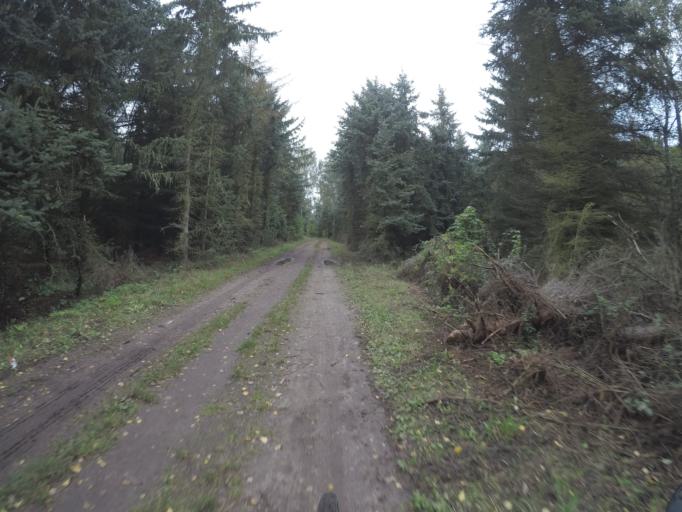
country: DE
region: Berlin
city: Buch
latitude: 52.6546
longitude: 13.4920
